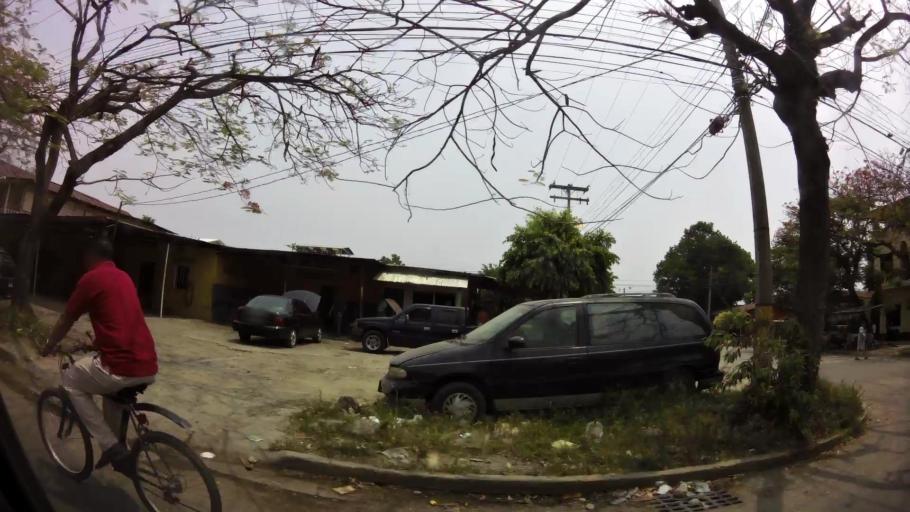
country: HN
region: Cortes
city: San Pedro Sula
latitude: 15.4861
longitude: -88.0157
